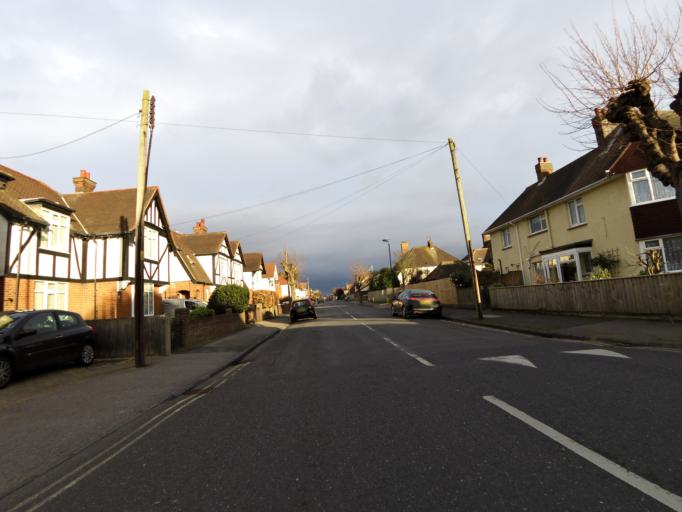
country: GB
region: England
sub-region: Suffolk
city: Felixstowe
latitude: 51.9645
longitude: 1.3468
